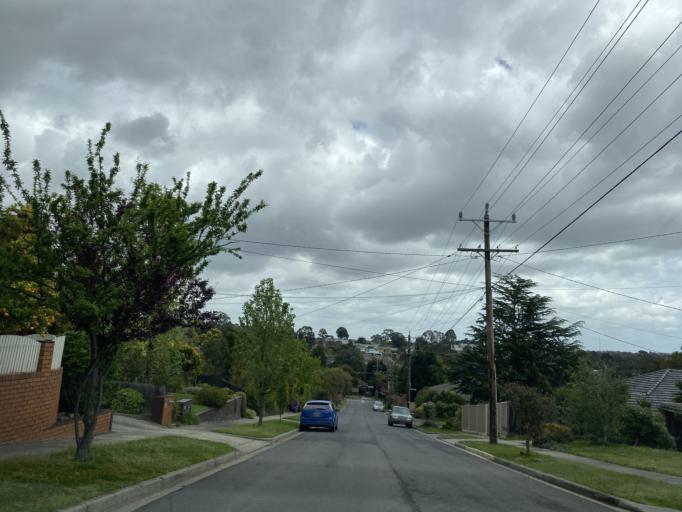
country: AU
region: Victoria
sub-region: Banyule
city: Darch
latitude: -37.7572
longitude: 145.1369
